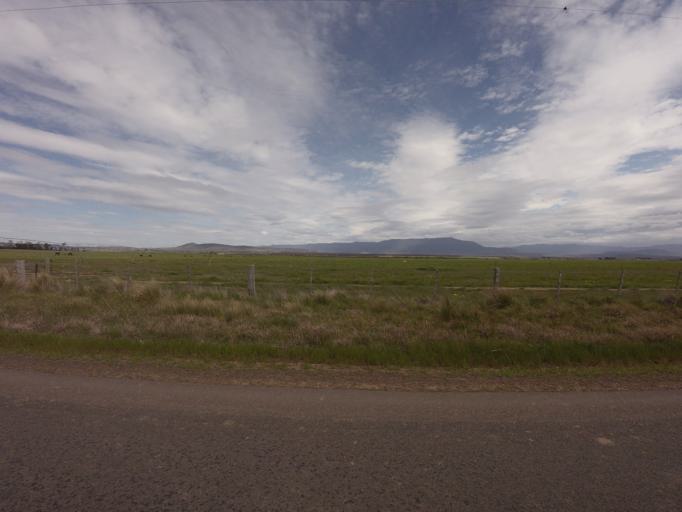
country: AU
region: Tasmania
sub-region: Northern Midlands
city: Evandale
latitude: -41.8202
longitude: 147.3083
